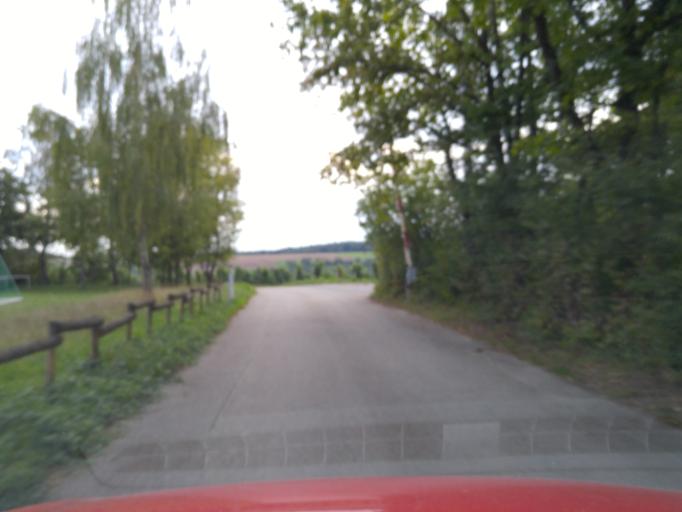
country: DE
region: Baden-Wuerttemberg
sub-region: Regierungsbezirk Stuttgart
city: Zaberfeld
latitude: 49.0258
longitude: 8.9248
